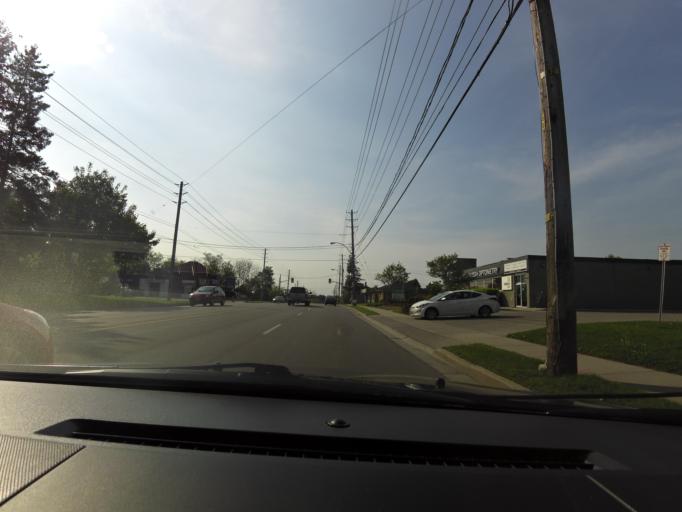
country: CA
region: Ontario
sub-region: Wellington County
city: Guelph
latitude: 43.5287
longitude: -80.2460
